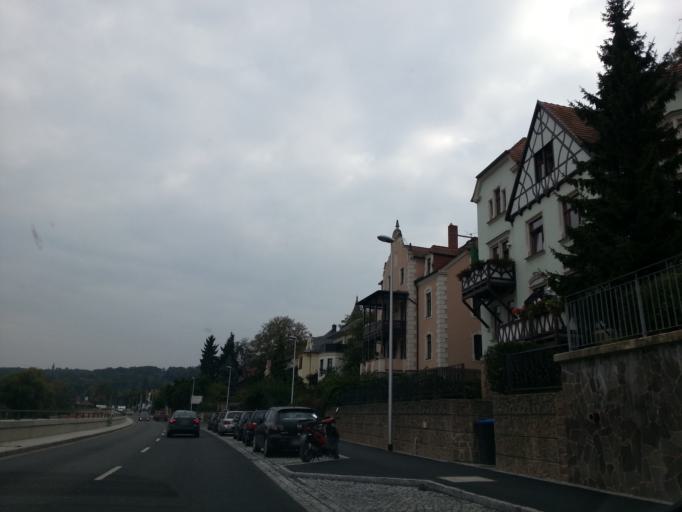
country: DE
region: Saxony
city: Meissen
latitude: 51.1565
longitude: 13.4785
